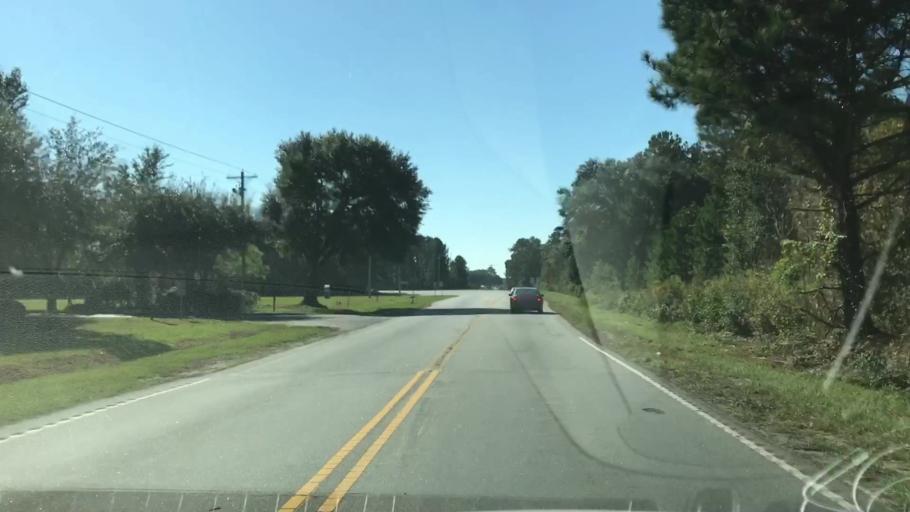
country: US
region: South Carolina
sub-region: Beaufort County
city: Bluffton
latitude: 32.3542
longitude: -80.9229
